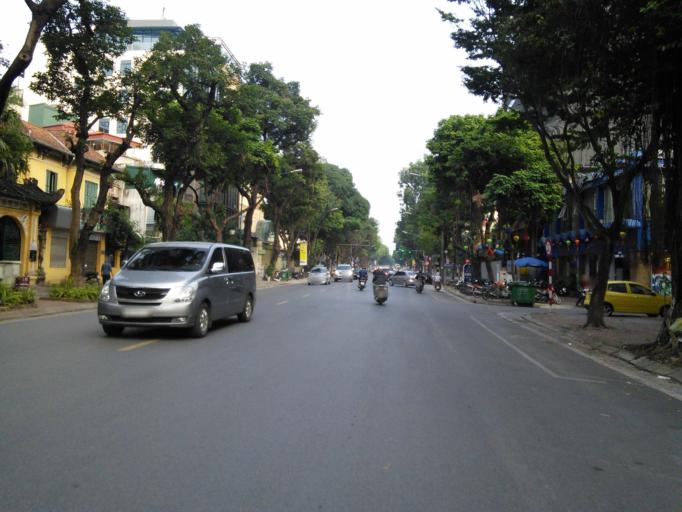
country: VN
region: Ha Noi
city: Hanoi
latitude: 21.0223
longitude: 105.8475
